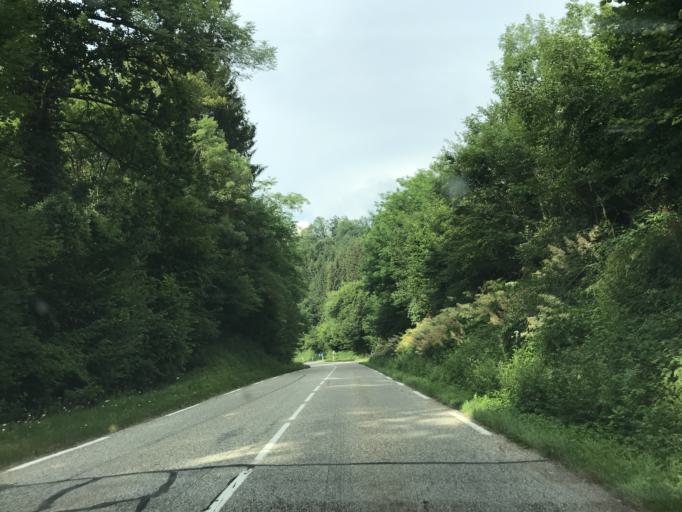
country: FR
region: Rhone-Alpes
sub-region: Departement de l'Isere
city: Allevard
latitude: 45.4160
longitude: 6.0896
